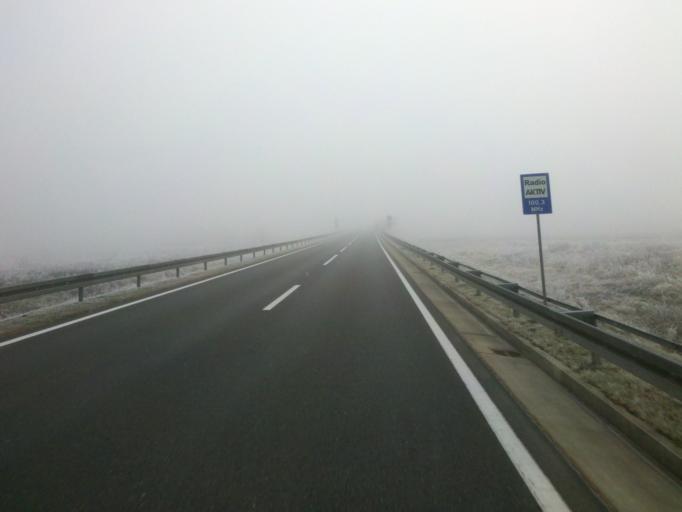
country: HR
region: Varazdinska
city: Nedeljanec
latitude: 46.2952
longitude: 16.3017
